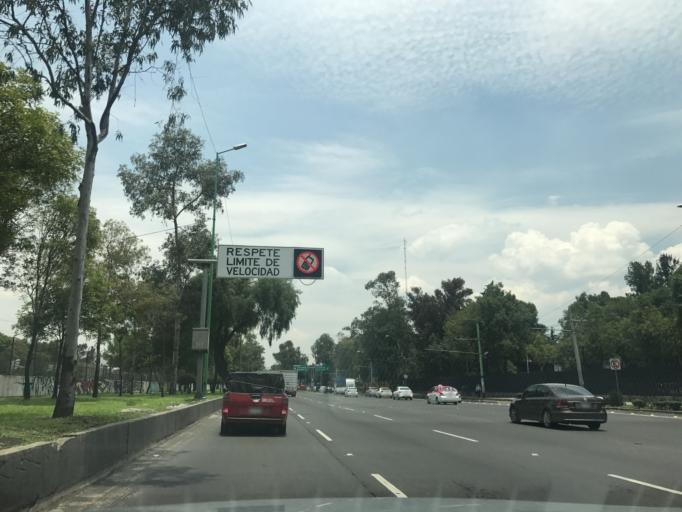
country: MX
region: Mexico
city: Colonia Lindavista
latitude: 19.4825
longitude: -99.1418
